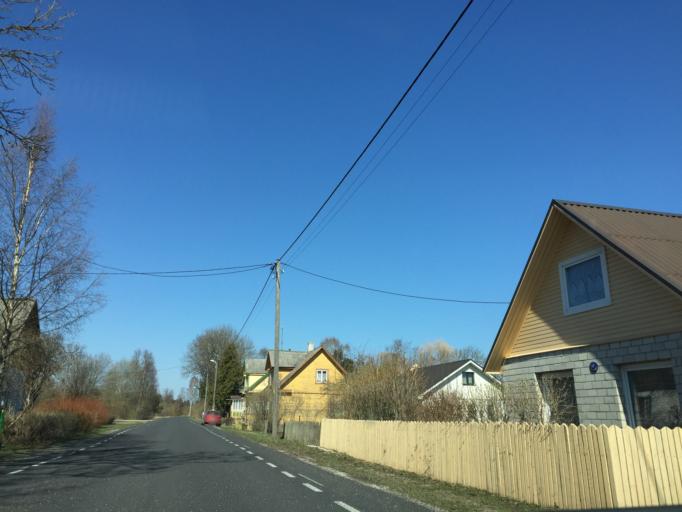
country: EE
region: Jogevamaa
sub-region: Mustvee linn
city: Mustvee
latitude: 58.8598
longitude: 26.9512
